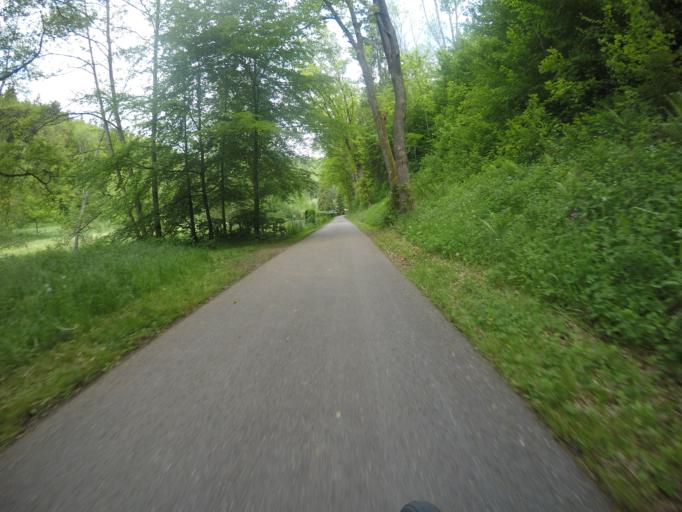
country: DE
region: Baden-Wuerttemberg
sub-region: Karlsruhe Region
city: Wildberg
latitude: 48.6091
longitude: 8.7361
